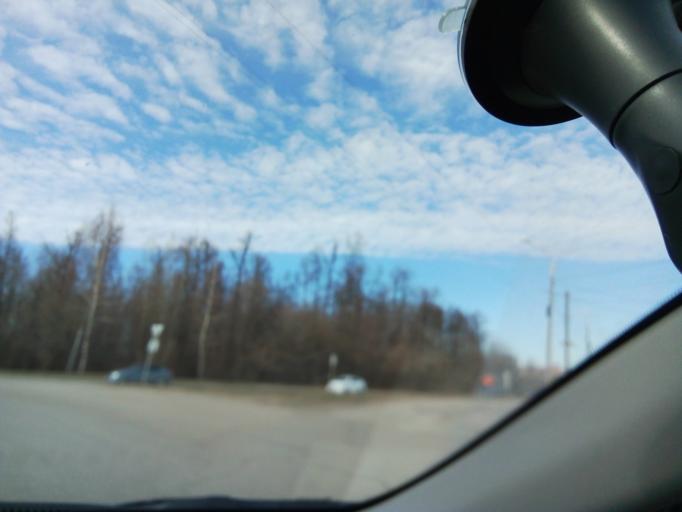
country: RU
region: Chuvashia
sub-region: Cheboksarskiy Rayon
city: Cheboksary
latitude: 56.0971
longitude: 47.2595
